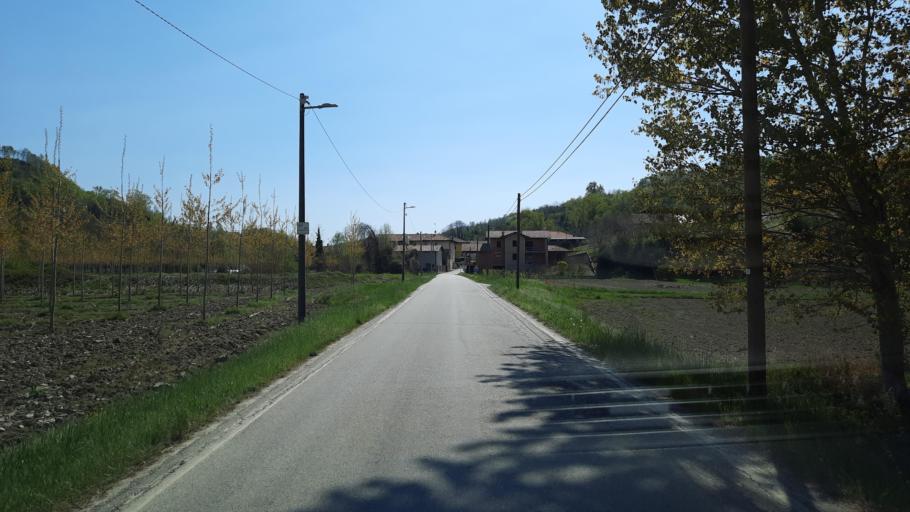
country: IT
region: Piedmont
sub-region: Provincia di Alessandria
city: Moncestino
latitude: 45.1608
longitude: 8.1327
